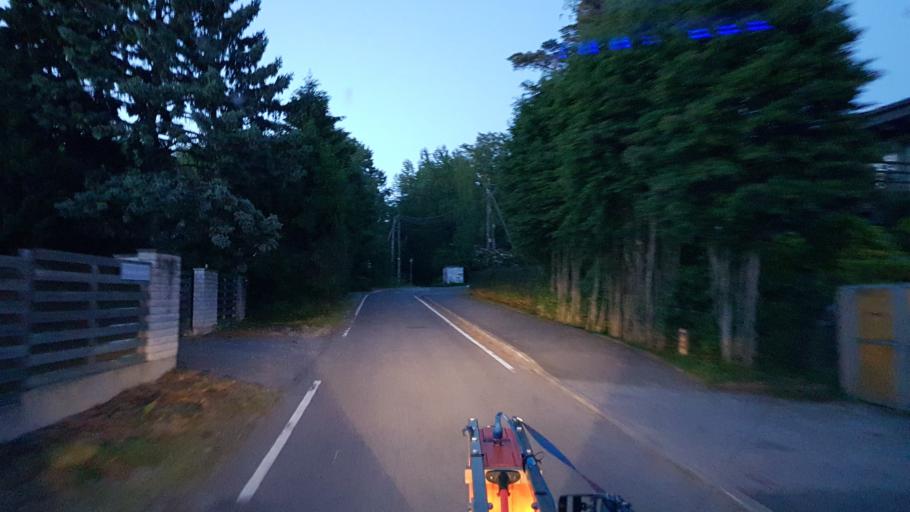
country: EE
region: Harju
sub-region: Harku vald
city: Tabasalu
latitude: 59.4593
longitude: 24.5712
